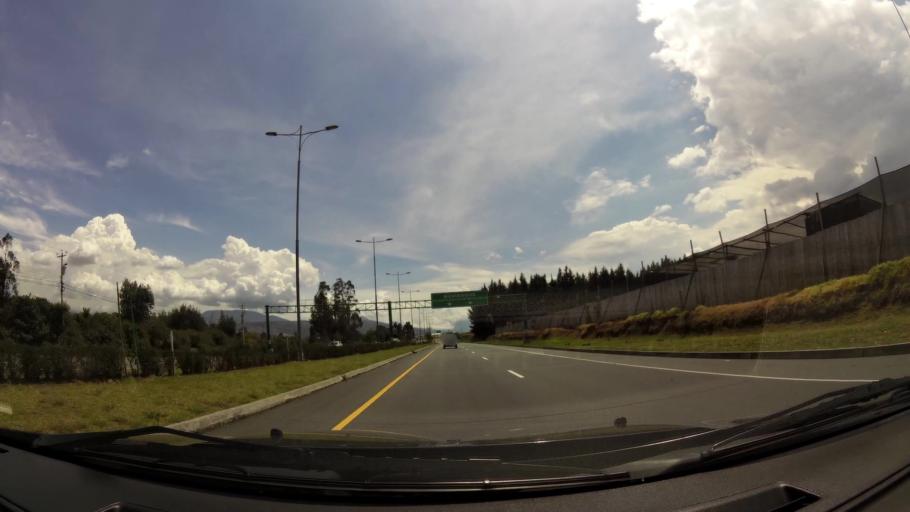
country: EC
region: Pichincha
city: Quito
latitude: -0.1590
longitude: -78.3478
